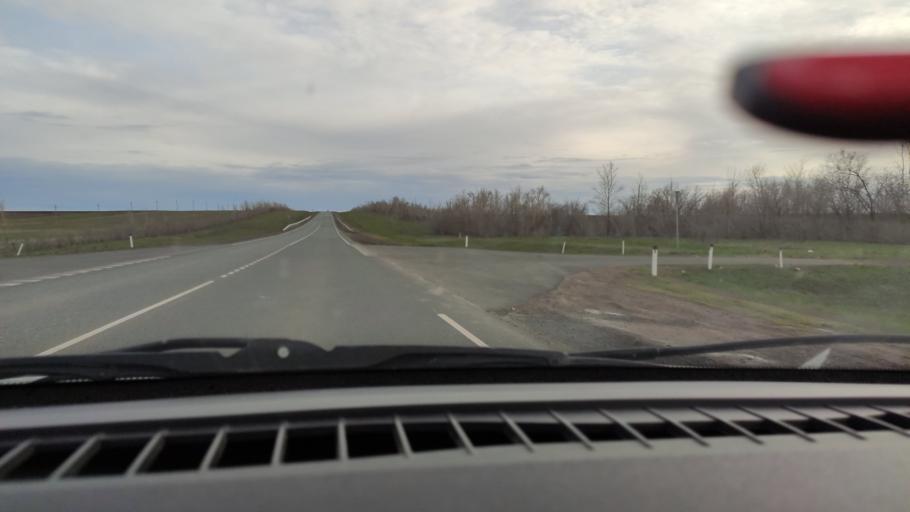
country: RU
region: Orenburg
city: Sakmara
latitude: 52.0761
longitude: 55.2649
